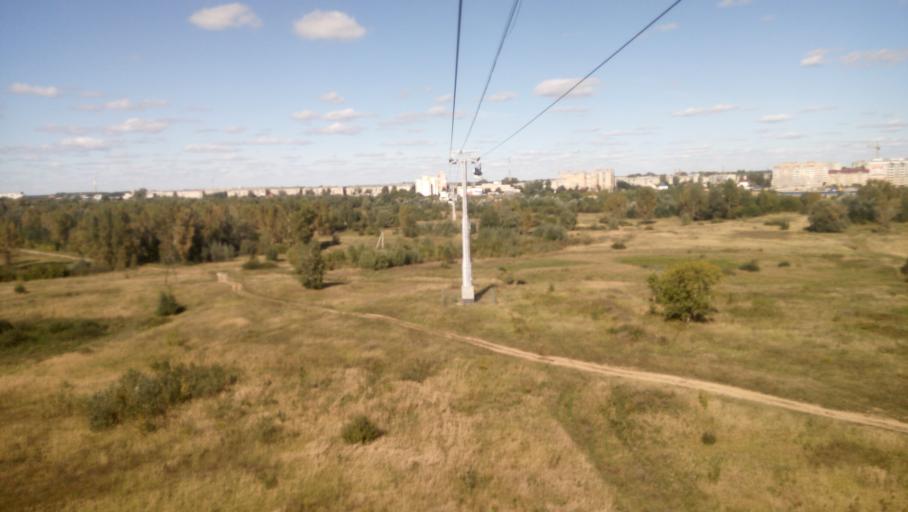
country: RU
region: Nizjnij Novgorod
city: Bor
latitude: 56.3455
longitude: 44.0550
